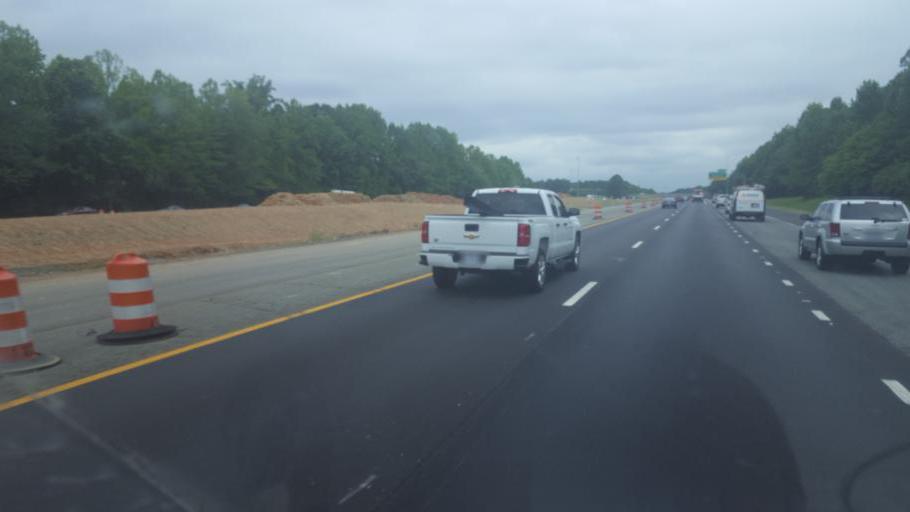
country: US
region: North Carolina
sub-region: Mecklenburg County
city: Huntersville
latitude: 35.4025
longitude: -80.8562
